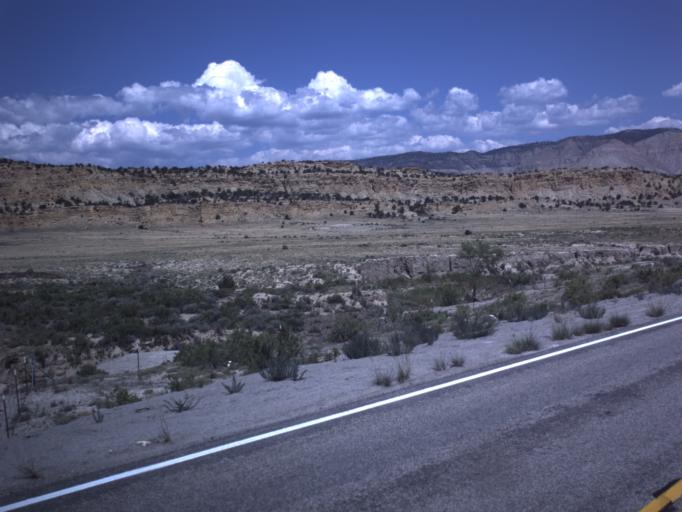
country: US
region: Utah
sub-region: Emery County
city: Ferron
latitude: 38.7850
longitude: -111.3505
